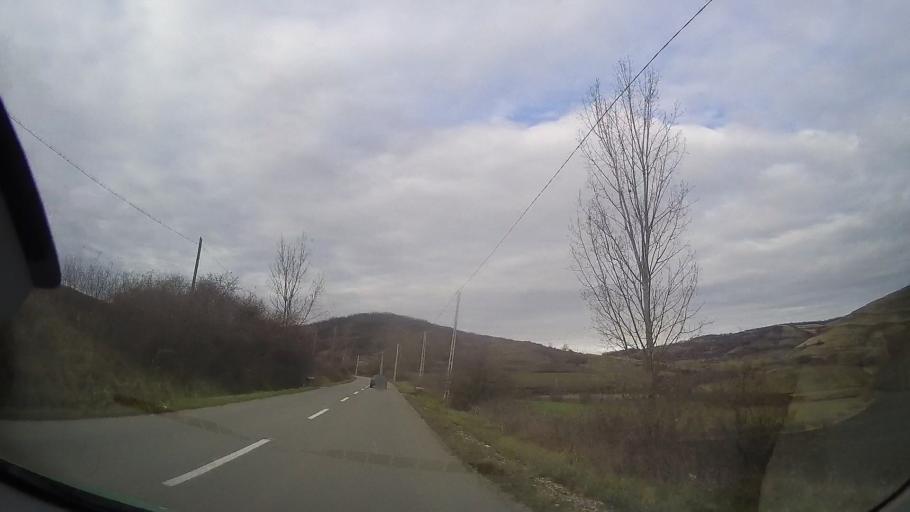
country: RO
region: Bistrita-Nasaud
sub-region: Comuna Milas
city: Milas
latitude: 46.8371
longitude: 24.4474
